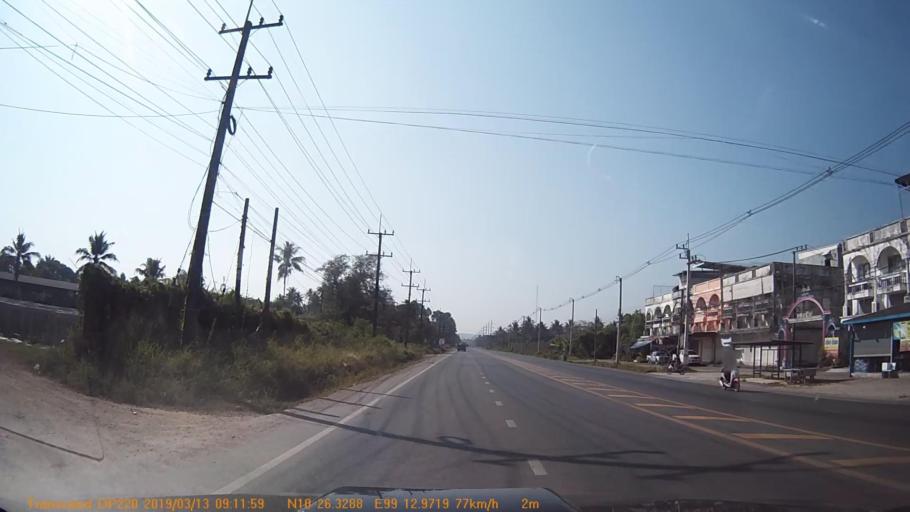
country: TH
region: Chumphon
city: Chumphon
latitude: 10.4386
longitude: 99.2163
